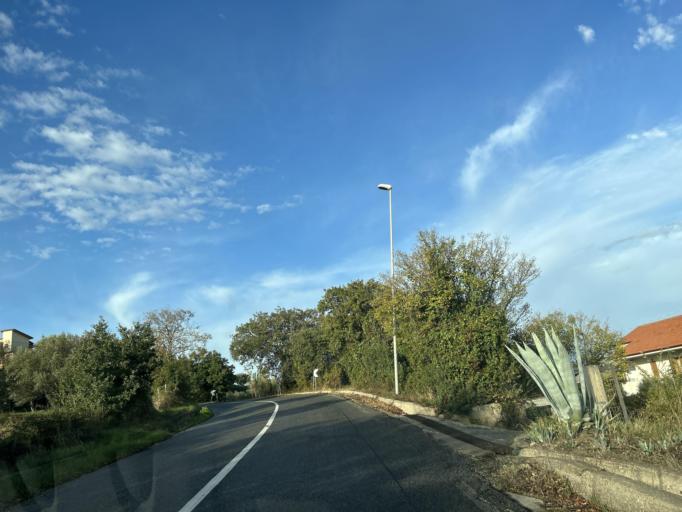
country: IT
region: Calabria
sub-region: Provincia di Catanzaro
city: Staletti
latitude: 38.7676
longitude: 16.5245
